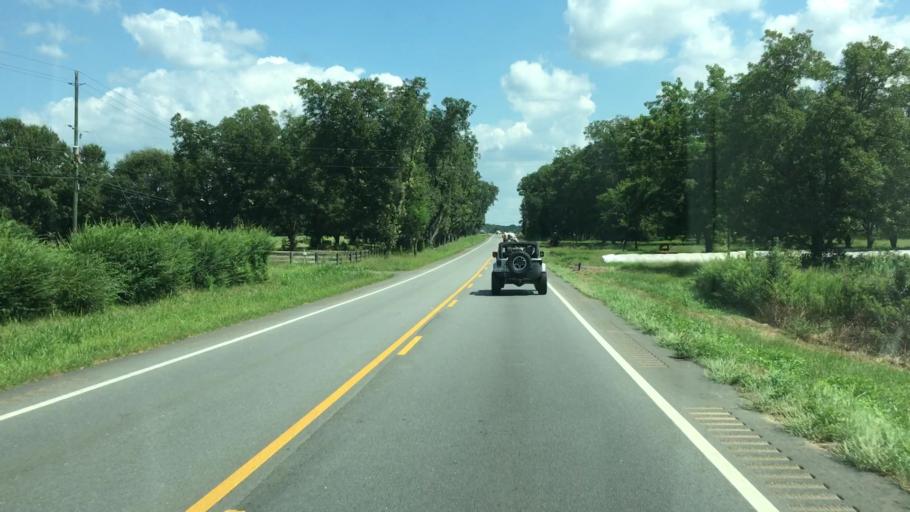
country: US
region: Georgia
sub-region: Morgan County
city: Madison
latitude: 33.5439
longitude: -83.4683
